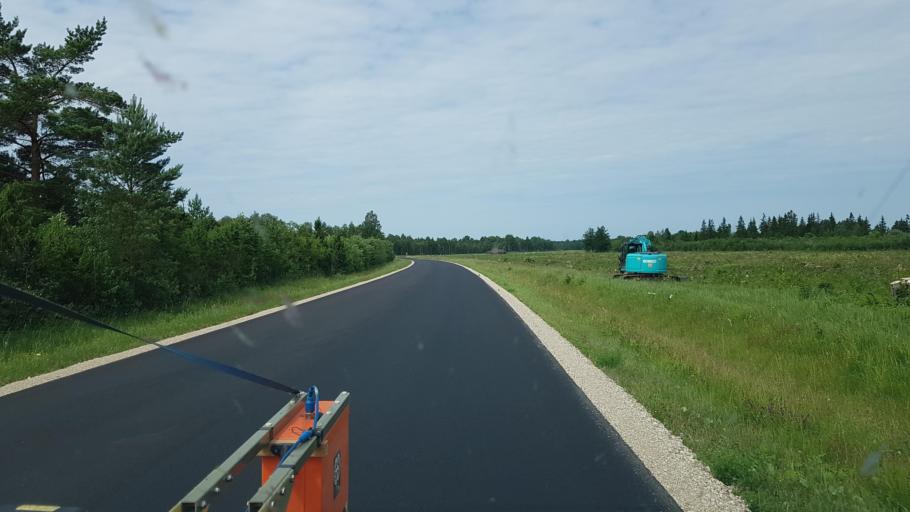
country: EE
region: Paernumaa
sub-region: Halinga vald
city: Parnu-Jaagupi
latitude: 58.6195
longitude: 24.2866
